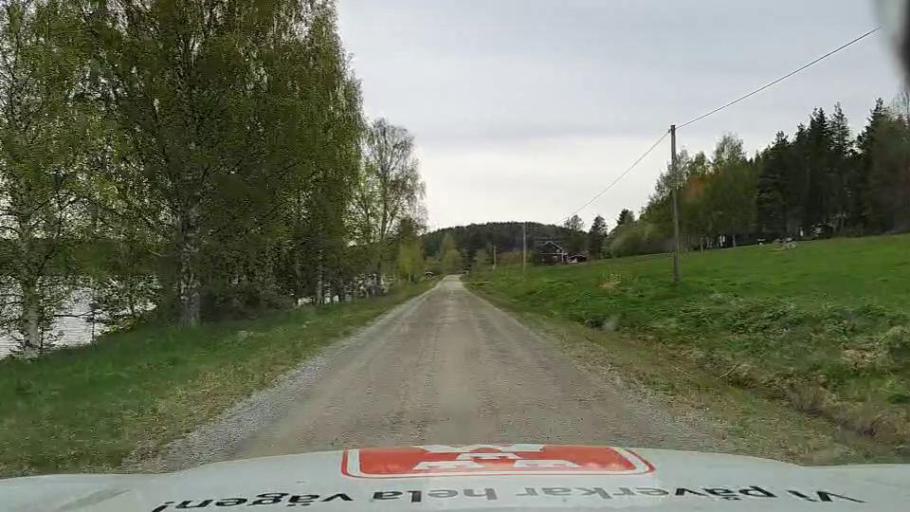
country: SE
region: Jaemtland
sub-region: Bergs Kommun
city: Hoverberg
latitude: 62.6849
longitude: 14.7916
